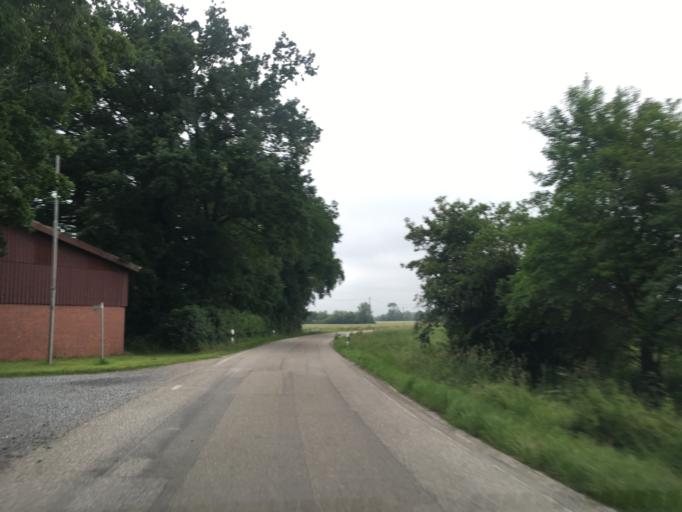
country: DE
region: North Rhine-Westphalia
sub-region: Regierungsbezirk Munster
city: Altenberge
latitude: 52.0226
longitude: 7.4604
